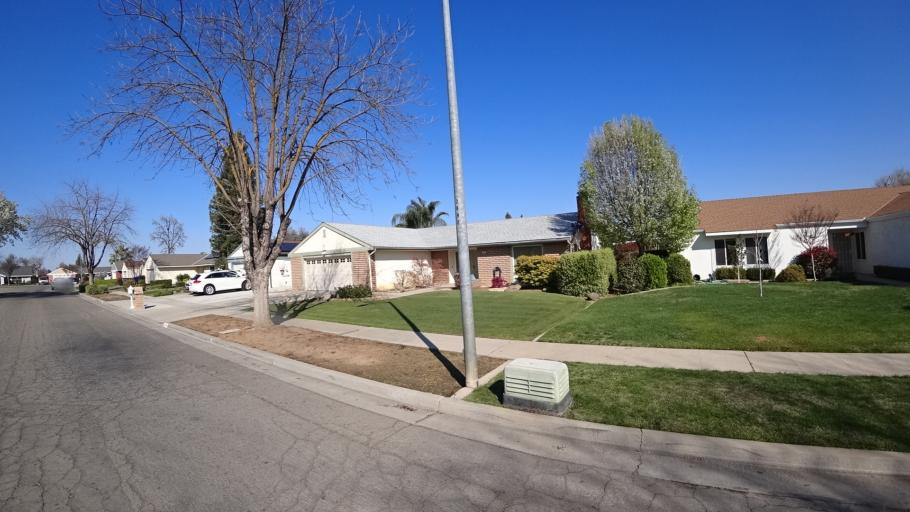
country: US
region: California
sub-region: Fresno County
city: Clovis
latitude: 36.8335
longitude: -119.7320
